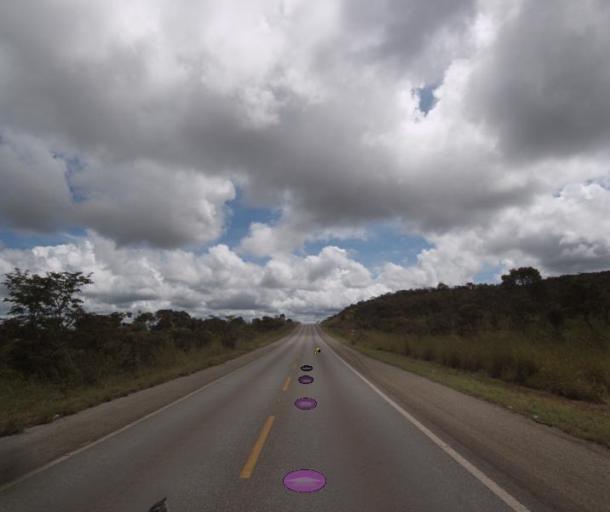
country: BR
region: Goias
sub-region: Pirenopolis
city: Pirenopolis
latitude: -15.7529
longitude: -48.5894
